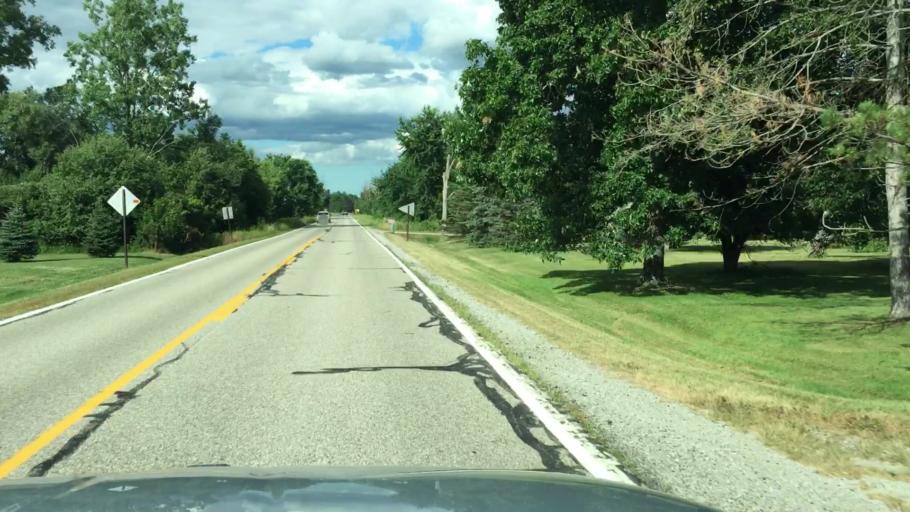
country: US
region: Michigan
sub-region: Saint Clair County
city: Capac
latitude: 43.1075
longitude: -82.9058
